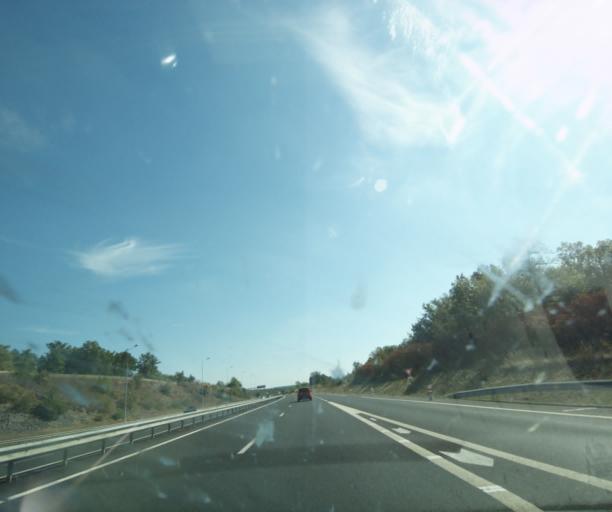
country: FR
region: Limousin
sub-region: Departement de la Correze
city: Cosnac
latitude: 45.0288
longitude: 1.5287
